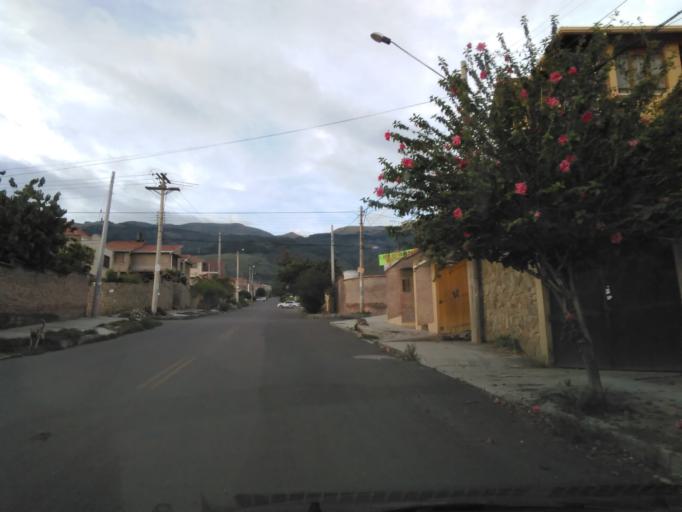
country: BO
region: Cochabamba
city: Cochabamba
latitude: -17.3602
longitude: -66.1561
